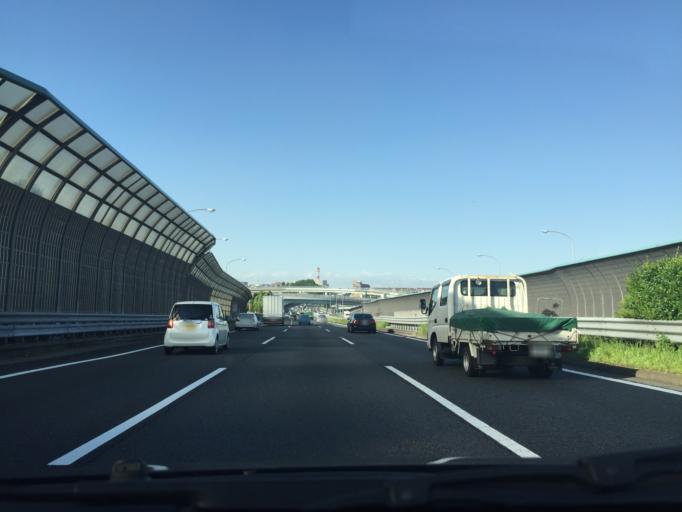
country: JP
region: Tokyo
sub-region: Machida-shi
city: Machida
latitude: 35.5388
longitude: 139.5360
